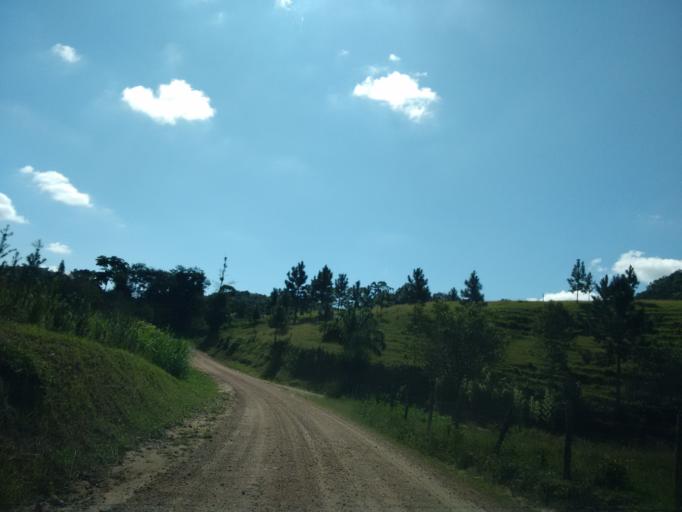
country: BR
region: Santa Catarina
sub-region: Indaial
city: Indaial
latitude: -26.9246
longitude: -49.1847
